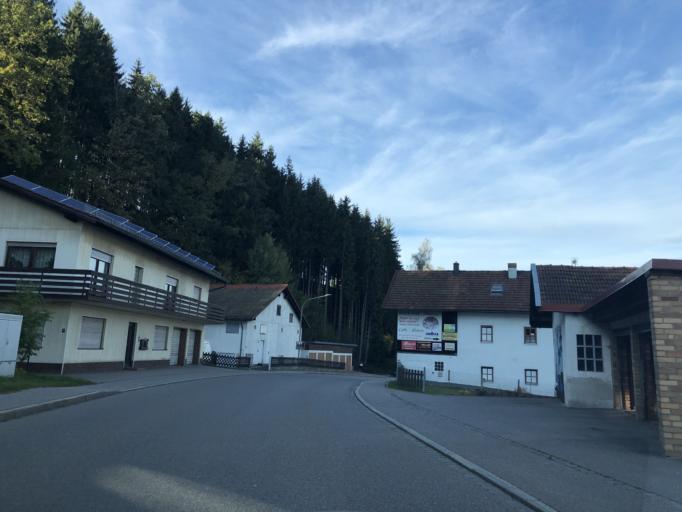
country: DE
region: Bavaria
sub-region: Lower Bavaria
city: Teisnach
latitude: 49.0360
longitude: 12.9944
